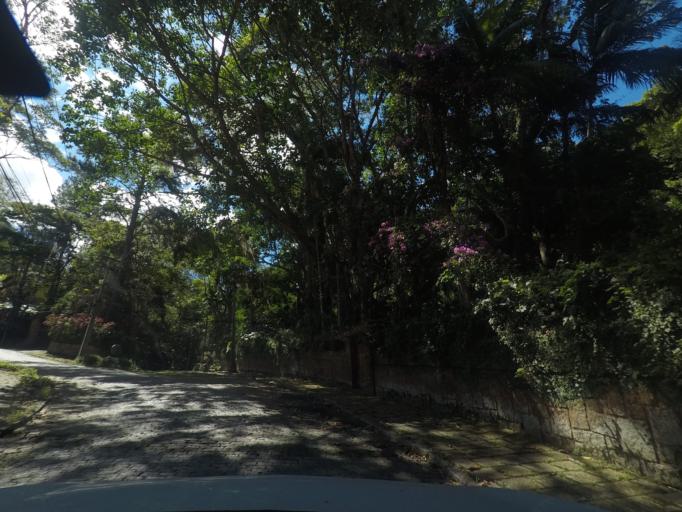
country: BR
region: Rio de Janeiro
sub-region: Teresopolis
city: Teresopolis
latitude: -22.4332
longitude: -42.9884
